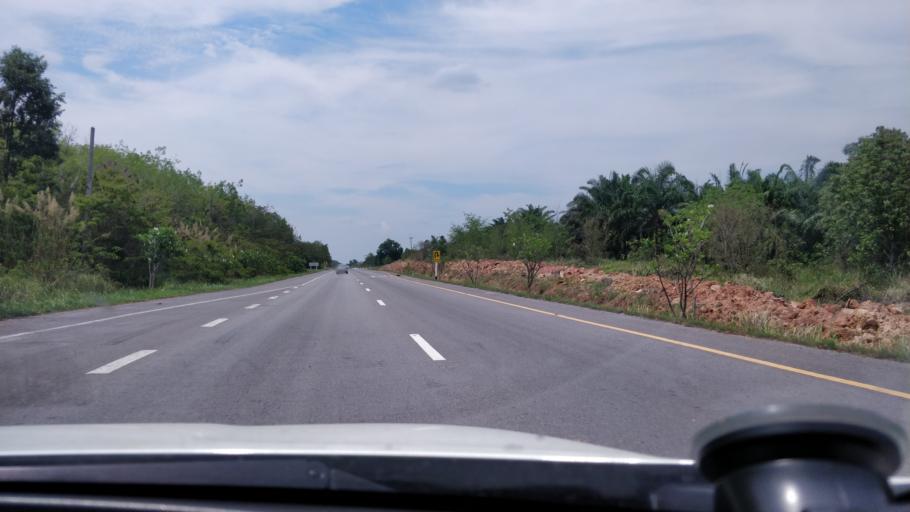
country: TH
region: Surat Thani
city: Khian Sa
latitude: 8.7413
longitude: 99.1606
